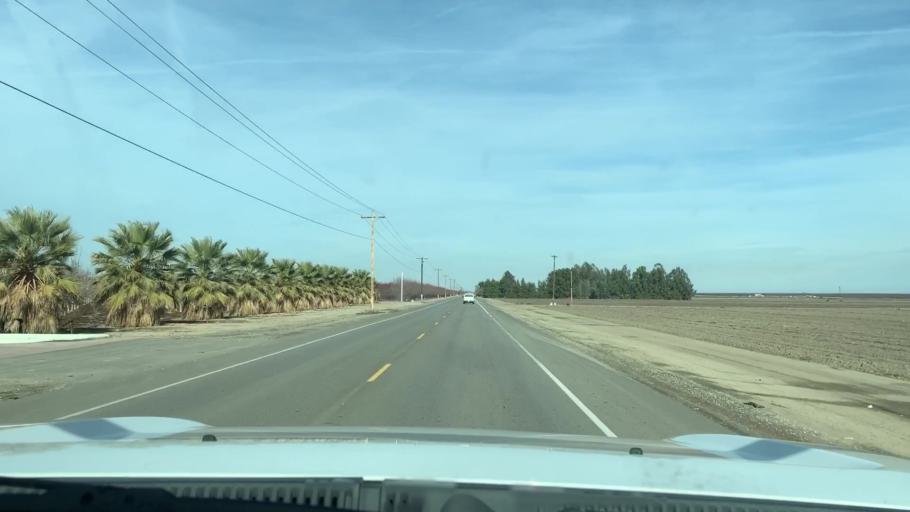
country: US
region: California
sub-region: Kern County
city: Buttonwillow
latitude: 35.5064
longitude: -119.4747
